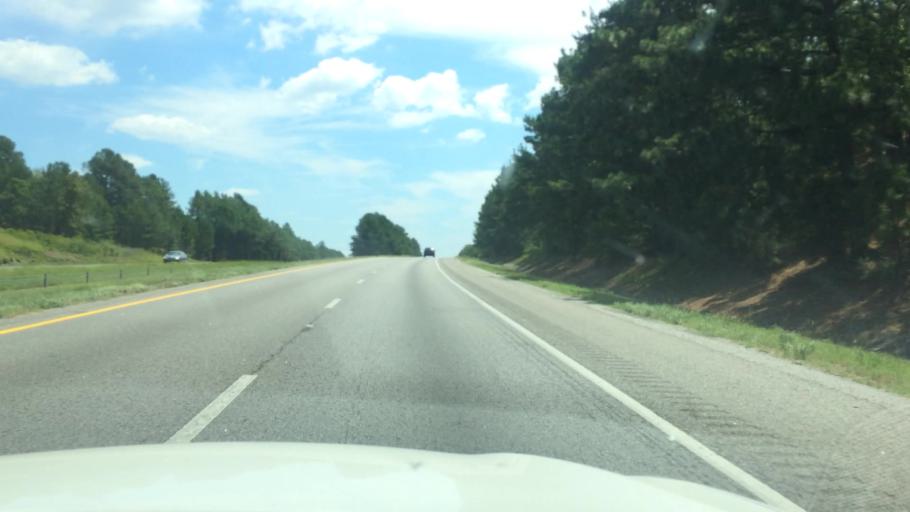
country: US
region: South Carolina
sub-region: Aiken County
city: Aiken
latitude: 33.7039
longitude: -81.5991
